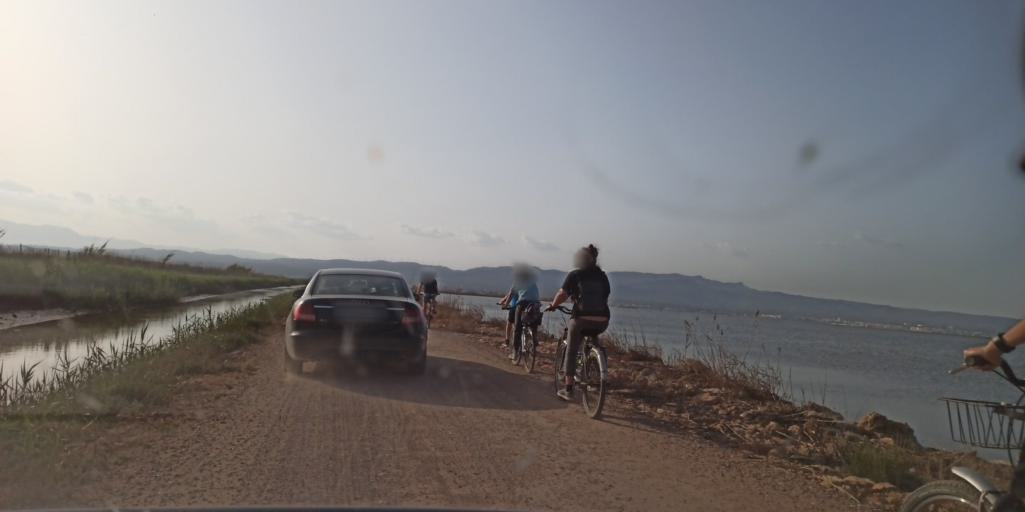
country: ES
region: Catalonia
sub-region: Provincia de Tarragona
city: L'Ampolla
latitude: 40.7678
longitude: 0.7346
